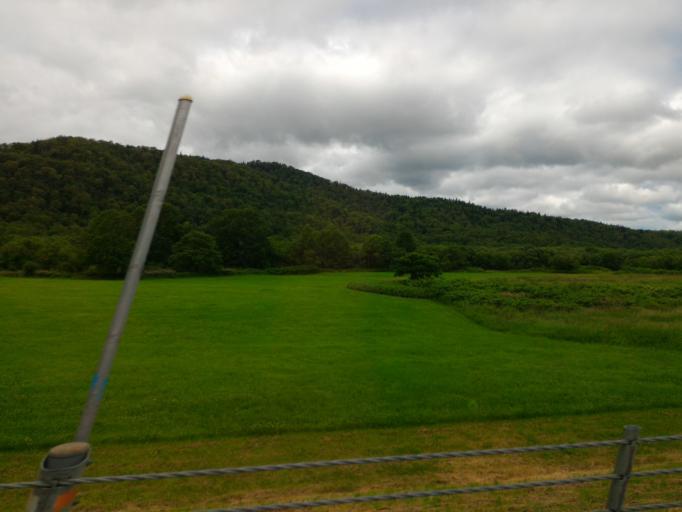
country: JP
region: Hokkaido
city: Nayoro
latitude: 44.7244
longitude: 142.2516
